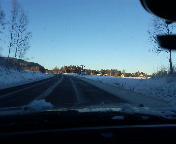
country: SE
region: Gaevleborg
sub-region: Bollnas Kommun
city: Arbra
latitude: 61.5353
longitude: 16.3633
